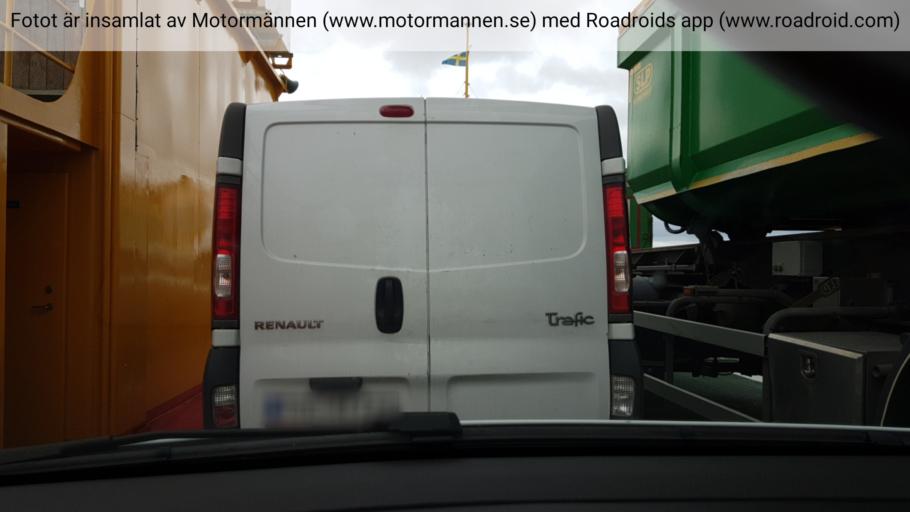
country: SE
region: Stockholm
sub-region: Vaxholms Kommun
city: Vaxholm
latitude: 59.4019
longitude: 18.3625
